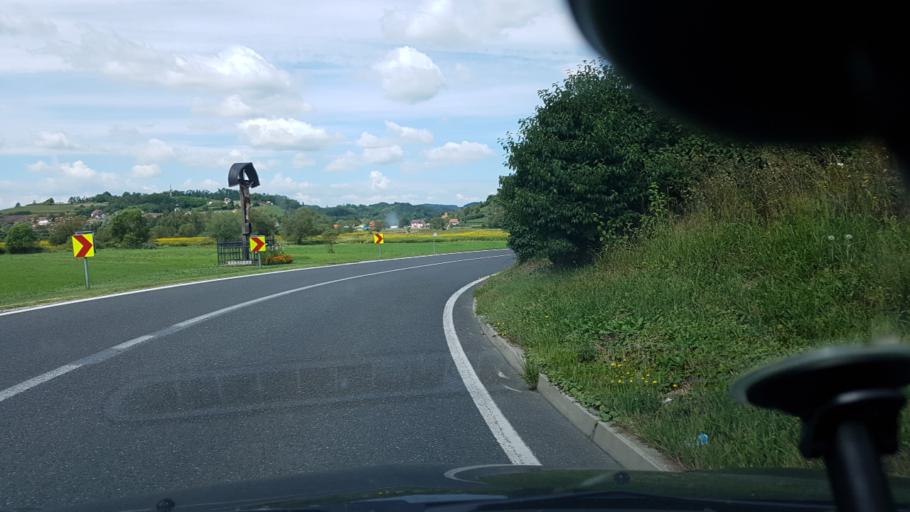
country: HR
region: Varazdinska
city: Lepoglava
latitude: 46.2231
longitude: 15.9930
